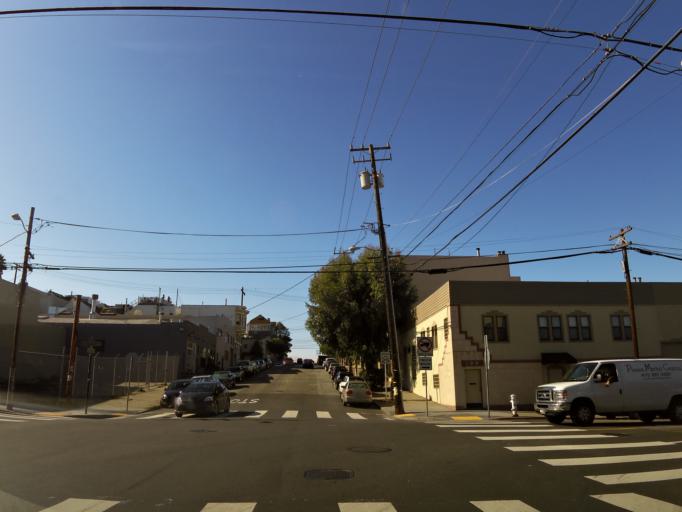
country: US
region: California
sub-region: San Francisco County
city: San Francisco
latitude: 37.7640
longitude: -122.3946
